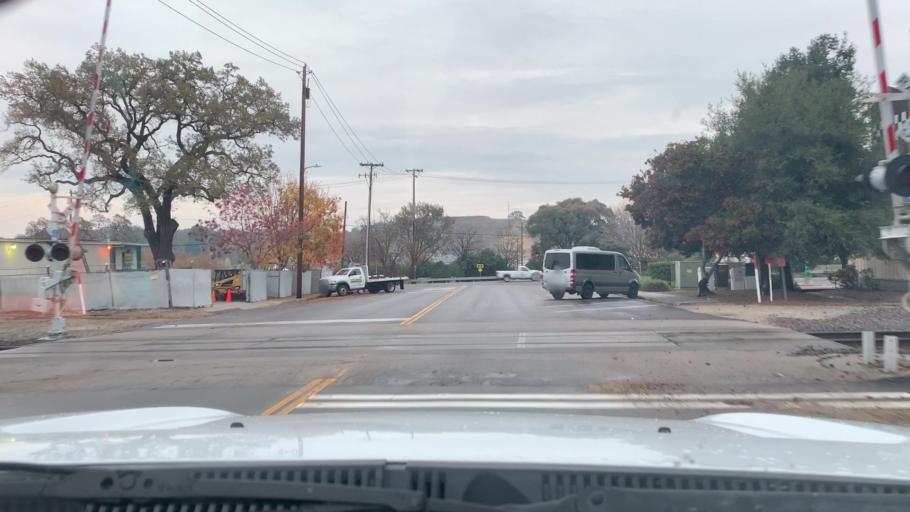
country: US
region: California
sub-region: San Luis Obispo County
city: Paso Robles
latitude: 35.6248
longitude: -120.6878
